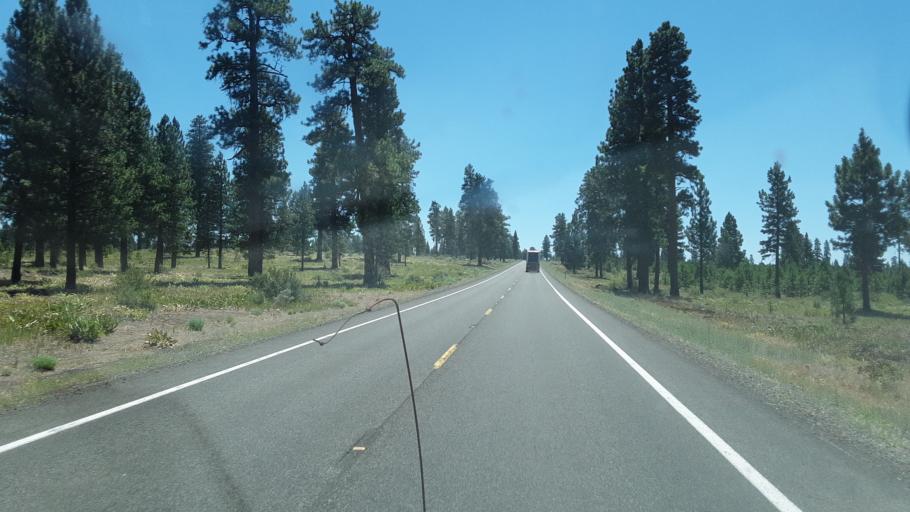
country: US
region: California
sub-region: Siskiyou County
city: Tulelake
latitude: 41.5869
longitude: -121.1942
